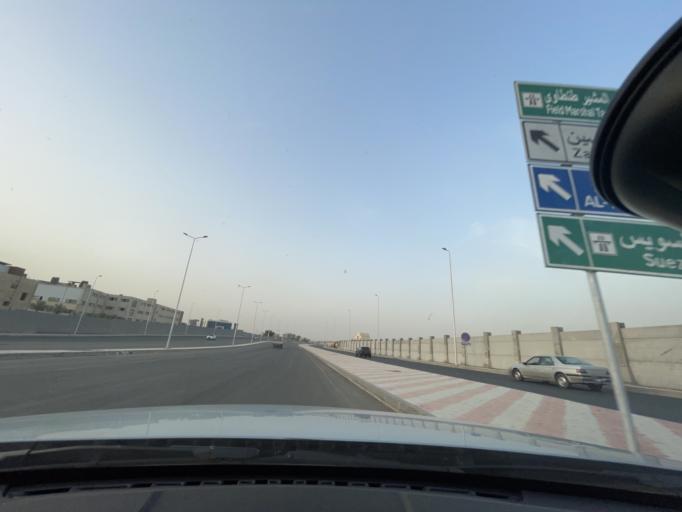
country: EG
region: Muhafazat al Qahirah
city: Cairo
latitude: 30.0260
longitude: 31.3467
